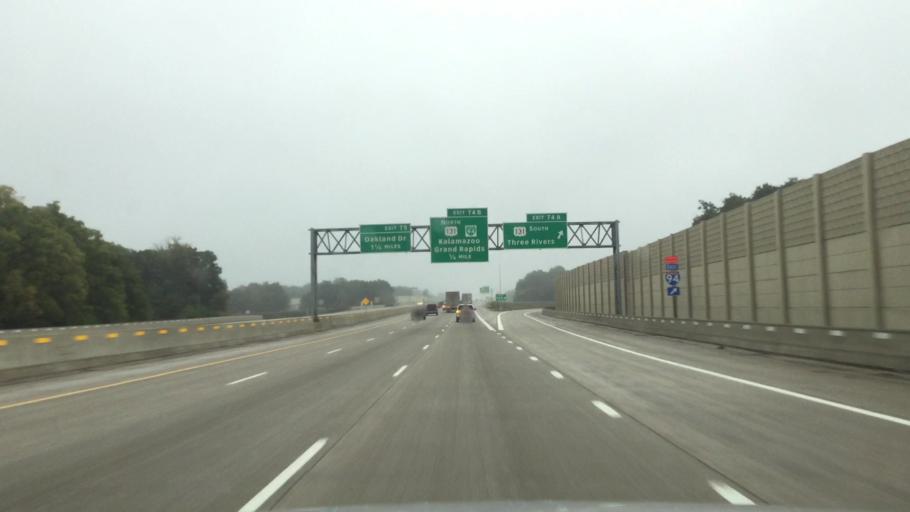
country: US
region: Michigan
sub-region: Kalamazoo County
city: Westwood
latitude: 42.2379
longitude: -85.6454
